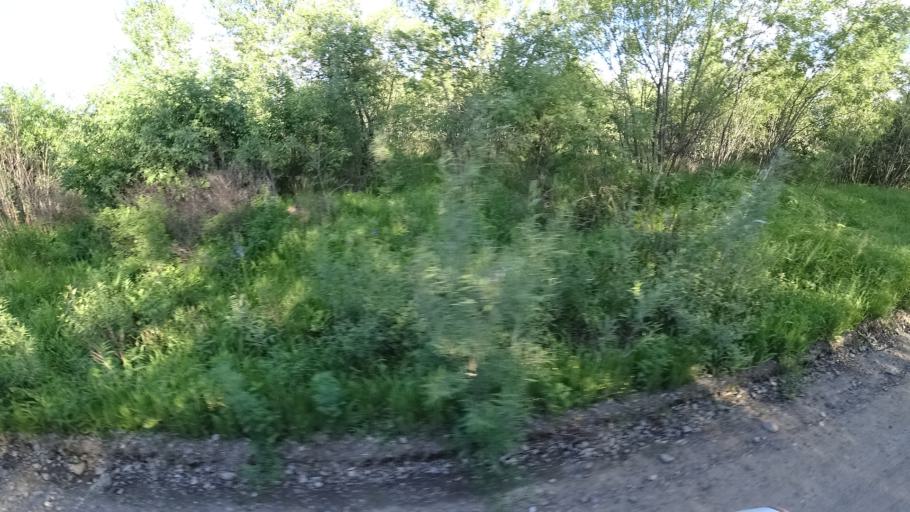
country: RU
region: Khabarovsk Krai
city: Khor
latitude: 47.8472
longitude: 134.9444
